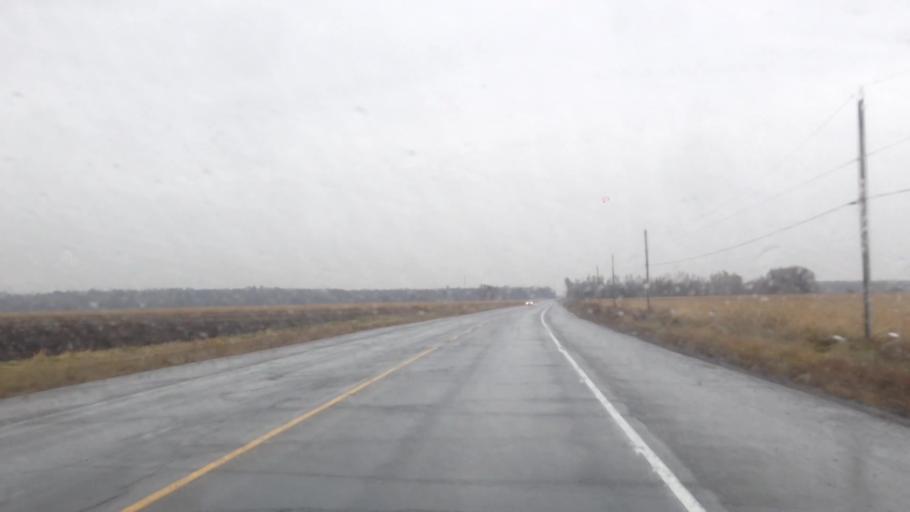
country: CA
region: Ontario
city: Clarence-Rockland
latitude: 45.4474
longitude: -75.4221
